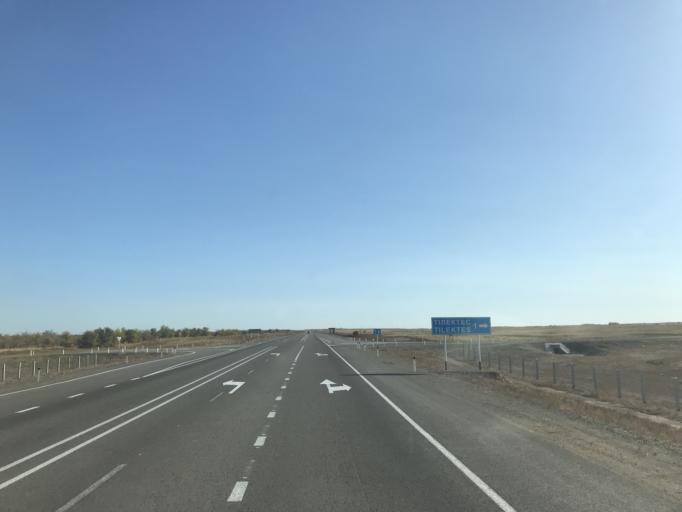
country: KZ
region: Pavlodar
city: Koktobe
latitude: 51.8149
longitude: 77.4706
